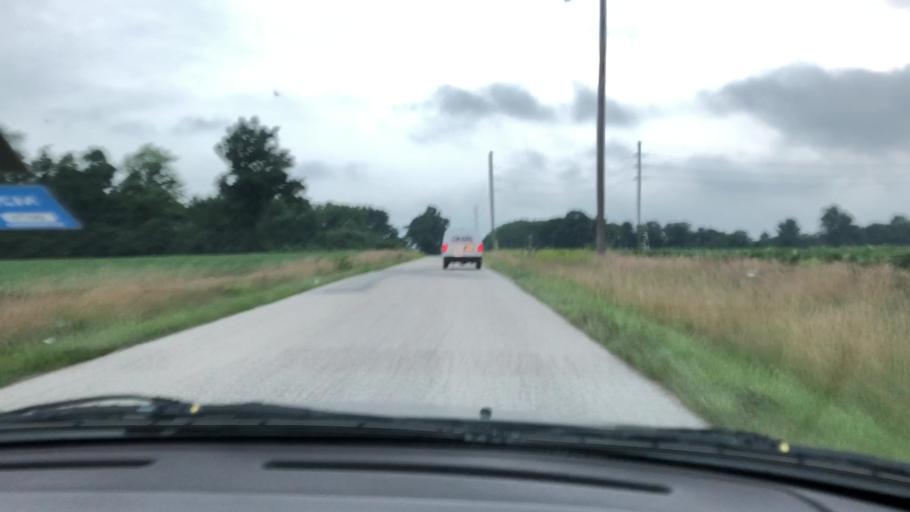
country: US
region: Indiana
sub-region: Greene County
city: Linton
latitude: 38.9776
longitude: -87.2981
